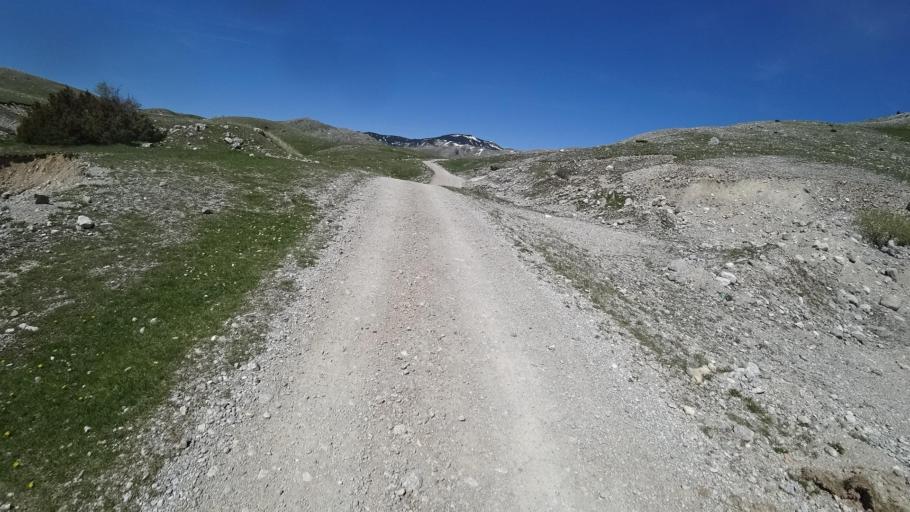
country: BA
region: Federation of Bosnia and Herzegovina
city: Gracanica
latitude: 43.6853
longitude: 18.2311
